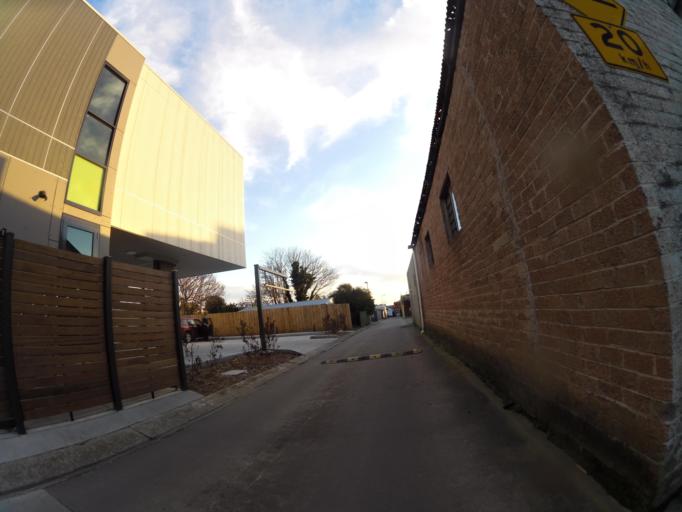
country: AU
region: Victoria
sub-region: Bass Coast
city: North Wonthaggi
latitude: -38.6064
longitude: 145.5936
